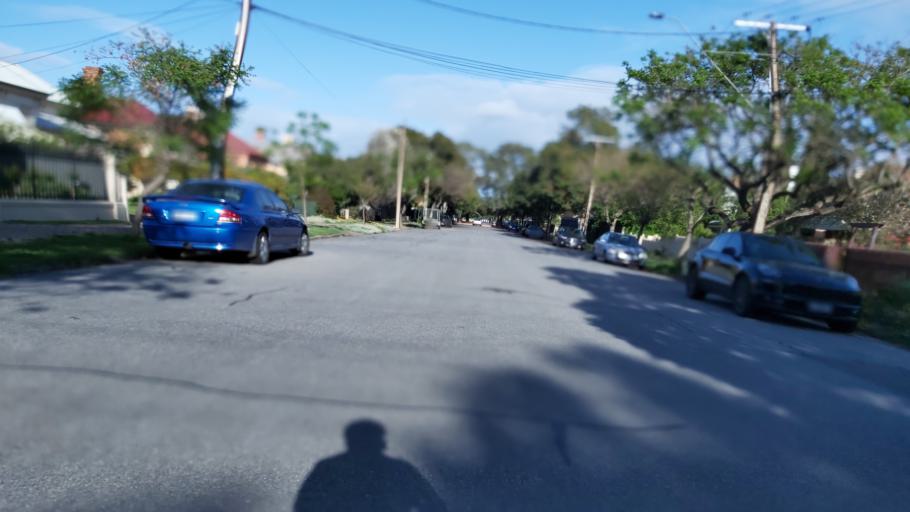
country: AU
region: South Australia
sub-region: Unley
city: Fullarton
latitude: -34.9490
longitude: 138.6160
